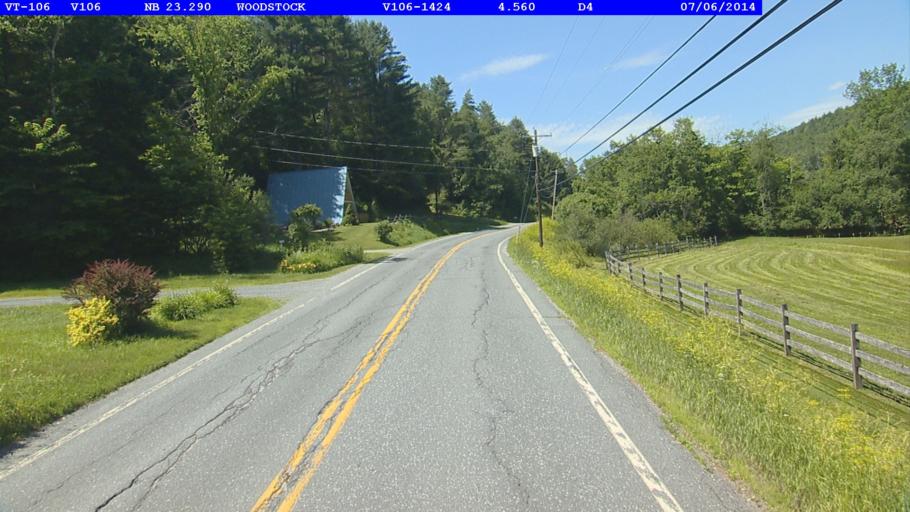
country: US
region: Vermont
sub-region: Windsor County
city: Woodstock
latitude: 43.5866
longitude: -72.5150
